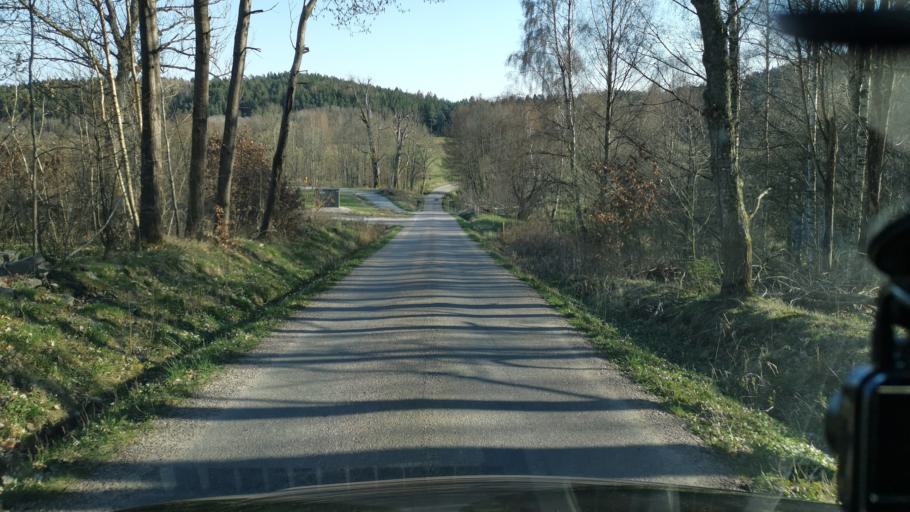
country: SE
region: Vaestra Goetaland
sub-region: Orust
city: Henan
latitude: 58.2786
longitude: 11.6397
